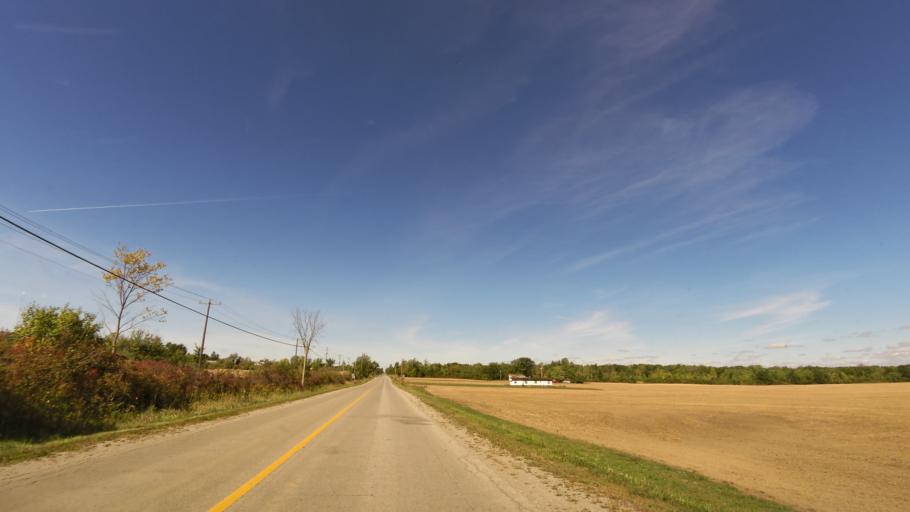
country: CA
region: Ontario
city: Ancaster
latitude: 43.0188
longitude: -80.0386
